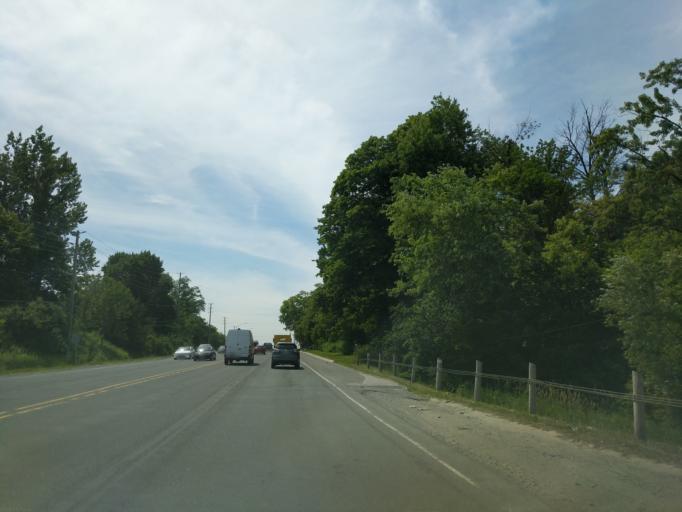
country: CA
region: Ontario
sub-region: York
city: Richmond Hill
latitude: 43.8642
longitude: -79.4715
